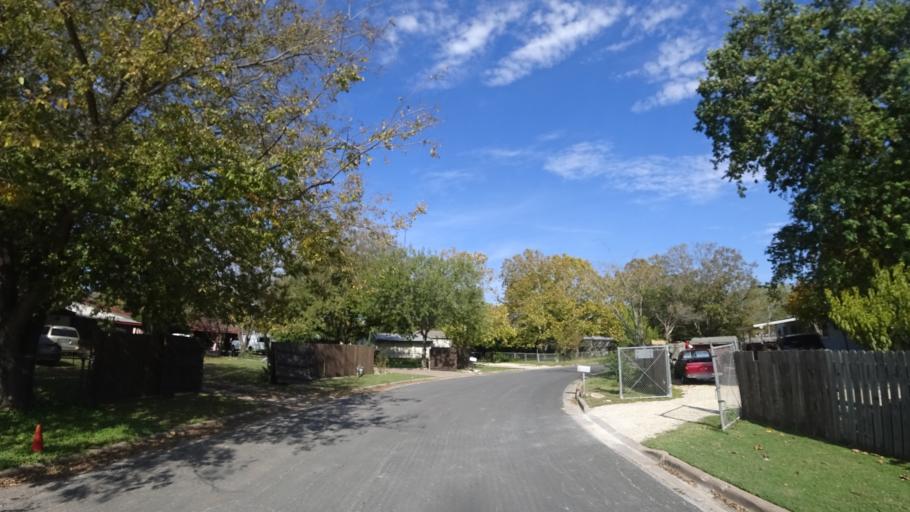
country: US
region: Texas
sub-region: Travis County
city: Pflugerville
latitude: 30.4076
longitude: -97.6290
